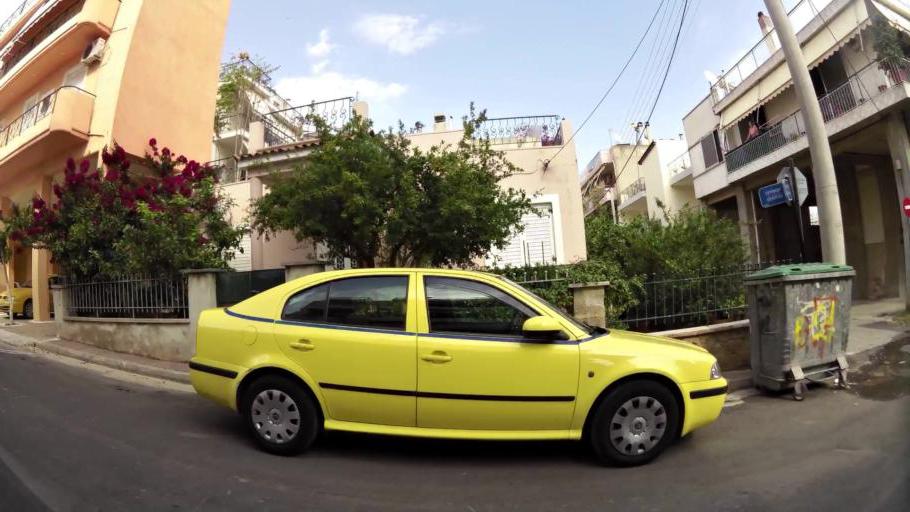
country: GR
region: Attica
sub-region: Nomarchia Athinas
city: Petroupolis
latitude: 38.0462
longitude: 23.6936
